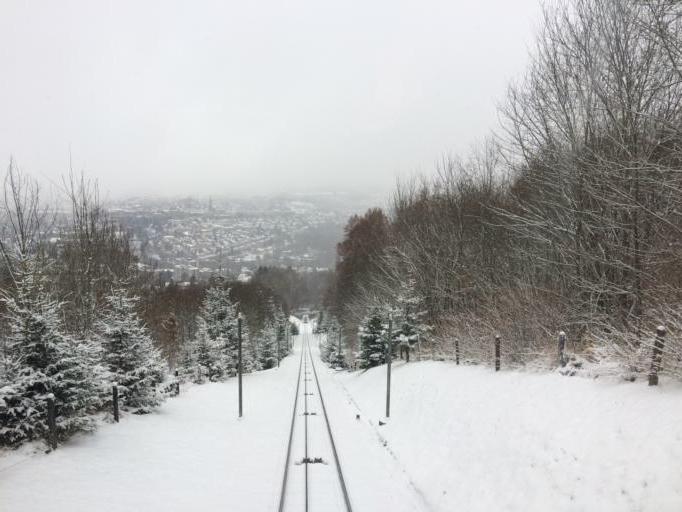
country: CH
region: Bern
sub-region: Bern-Mittelland District
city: Koniz
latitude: 46.9212
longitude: 7.4408
